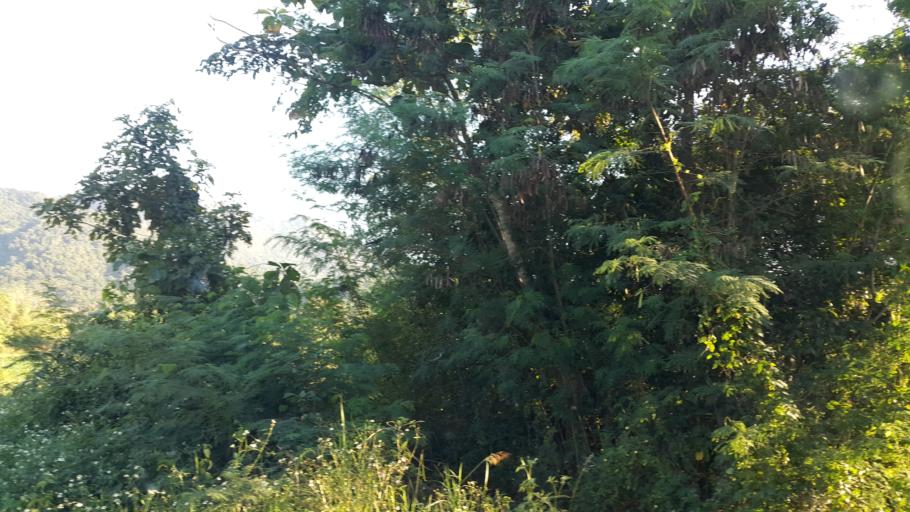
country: TH
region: Chiang Mai
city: Mae On
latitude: 18.7558
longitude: 99.2634
